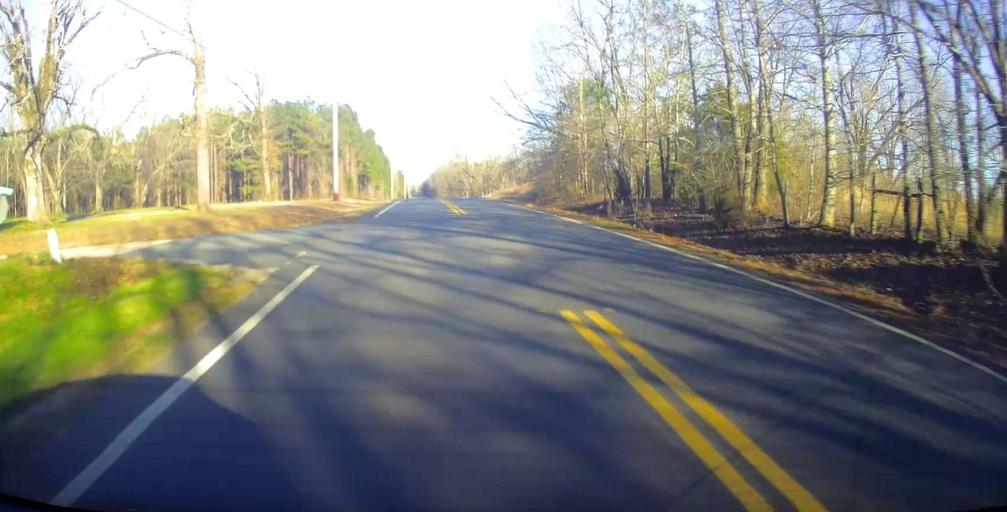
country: US
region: Georgia
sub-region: Harris County
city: Pine Mountain
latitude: 32.9162
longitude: -84.7887
